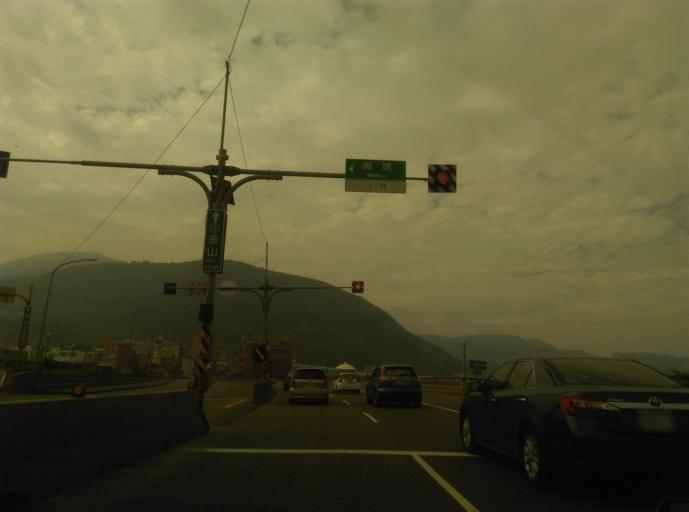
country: TW
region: Taiwan
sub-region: Keelung
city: Keelung
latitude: 25.1796
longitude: 121.6940
